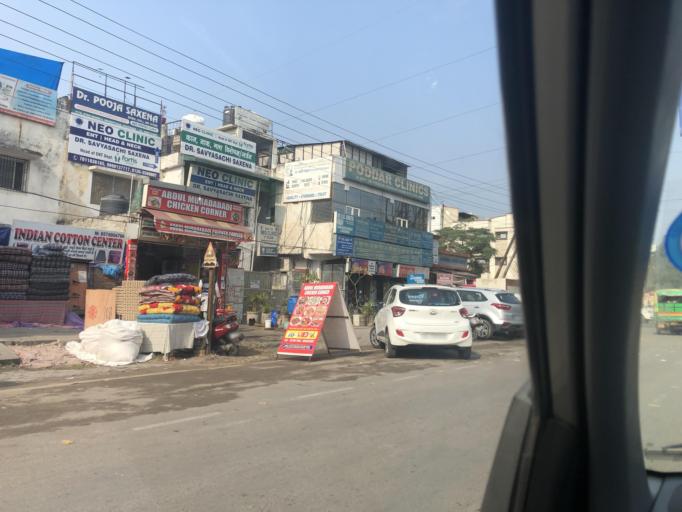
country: IN
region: Uttar Pradesh
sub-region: Gautam Buddha Nagar
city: Noida
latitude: 28.6464
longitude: 77.3597
